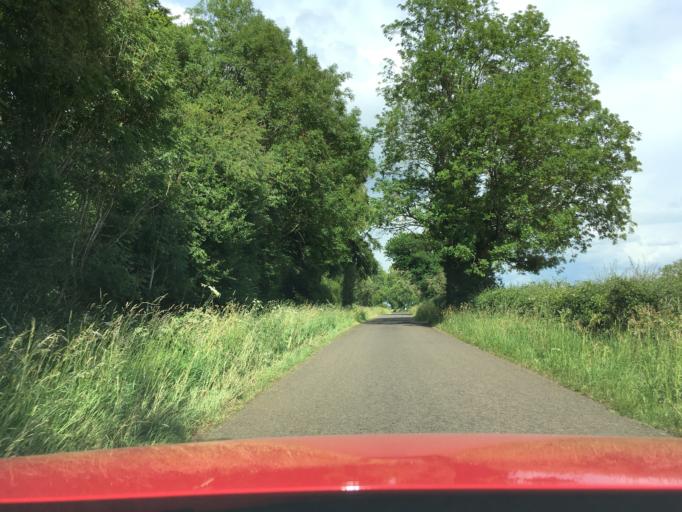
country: GB
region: England
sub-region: Gloucestershire
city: Chalford
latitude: 51.7076
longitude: -2.1018
